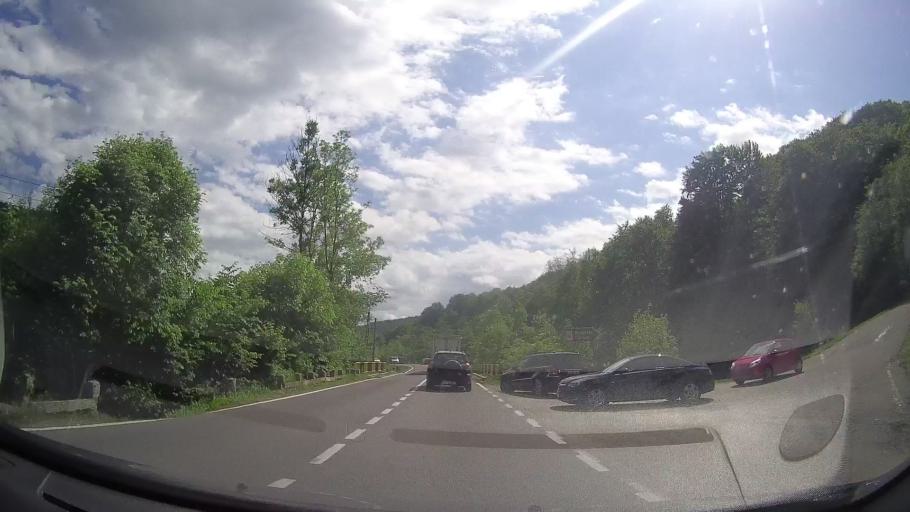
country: RO
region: Prahova
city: Maneciu
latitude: 45.3925
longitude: 25.9312
